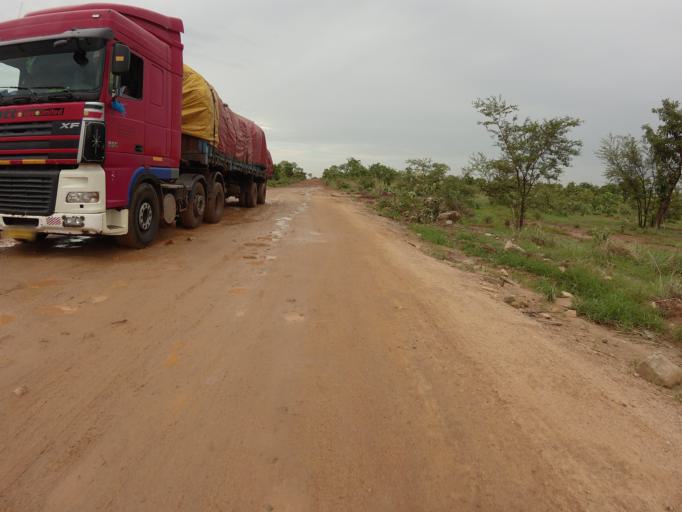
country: GH
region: Upper East
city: Bolgatanga
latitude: 10.8782
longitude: -0.6307
